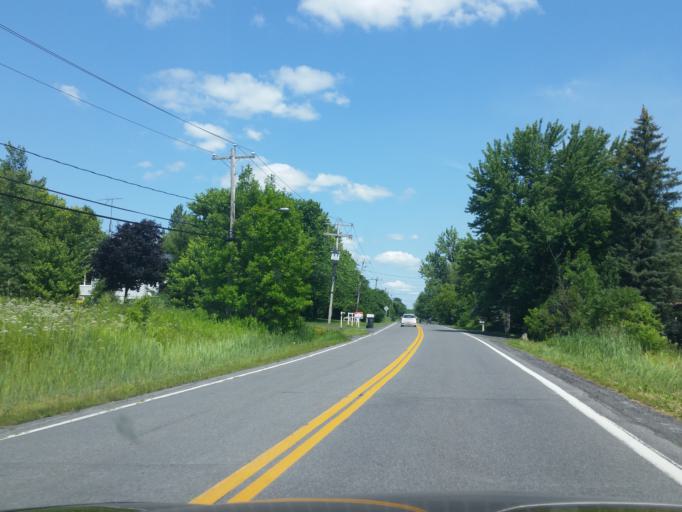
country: CA
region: Quebec
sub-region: Monteregie
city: Richelieu
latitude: 45.4167
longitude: -73.2456
